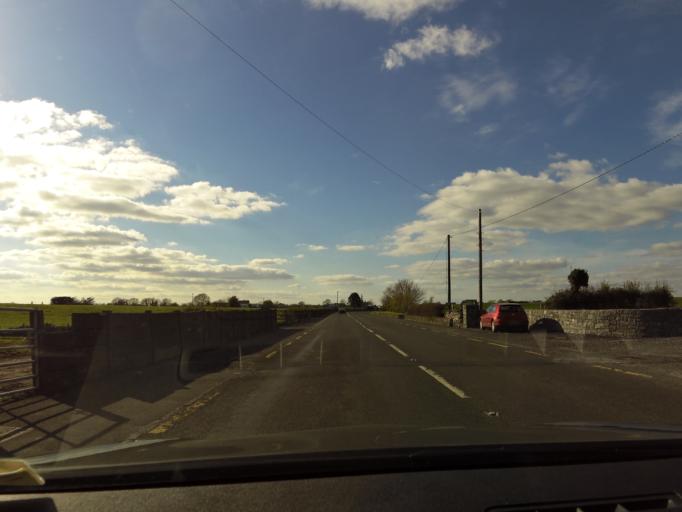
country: IE
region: Connaught
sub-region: County Galway
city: Portumna
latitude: 53.1002
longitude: -8.2299
